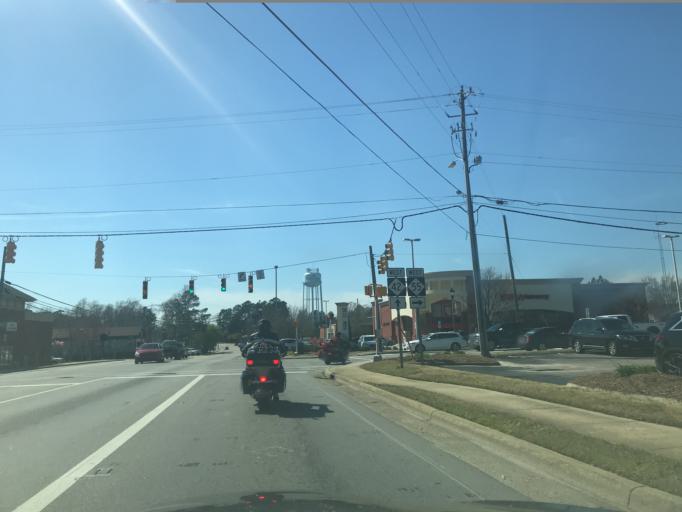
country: US
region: North Carolina
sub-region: Wake County
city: Fuquay-Varina
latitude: 35.5915
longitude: -78.7926
